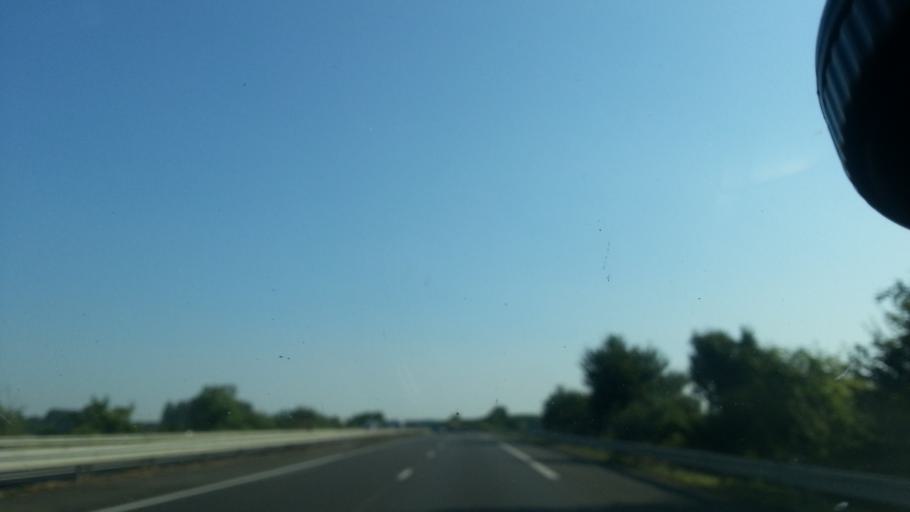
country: FR
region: Centre
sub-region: Departement d'Indre-et-Loire
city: La Celle-Saint-Avant
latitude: 47.0431
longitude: 0.5823
